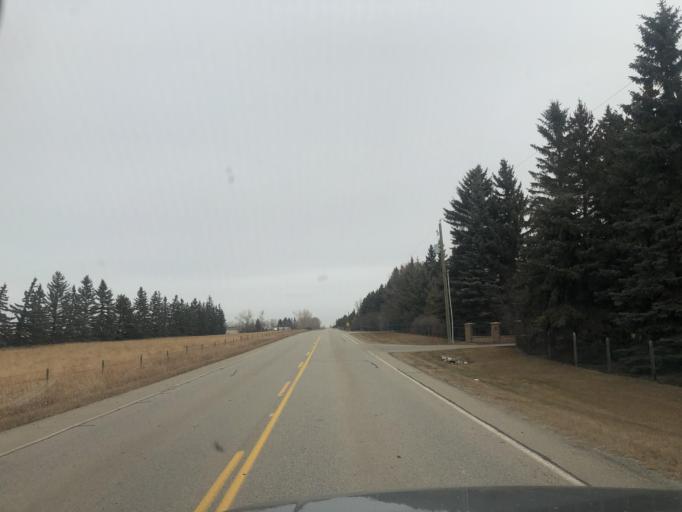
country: CA
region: Alberta
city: Chestermere
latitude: 50.9916
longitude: -113.8654
